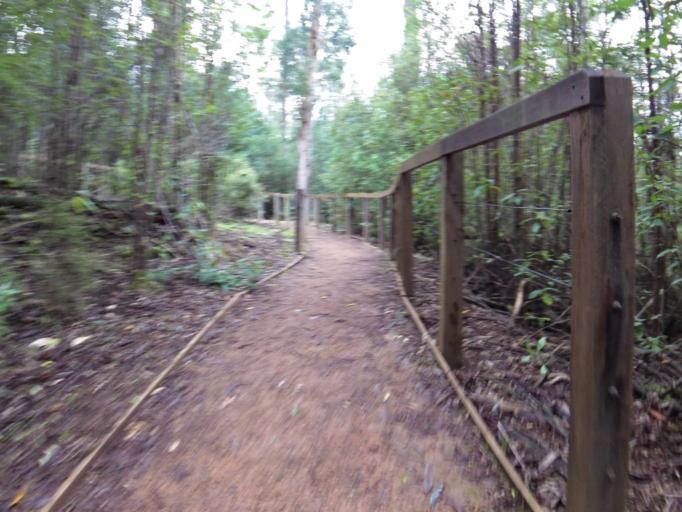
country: AU
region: Victoria
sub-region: Murrindindi
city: Kinglake West
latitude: -37.4925
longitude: 145.2484
